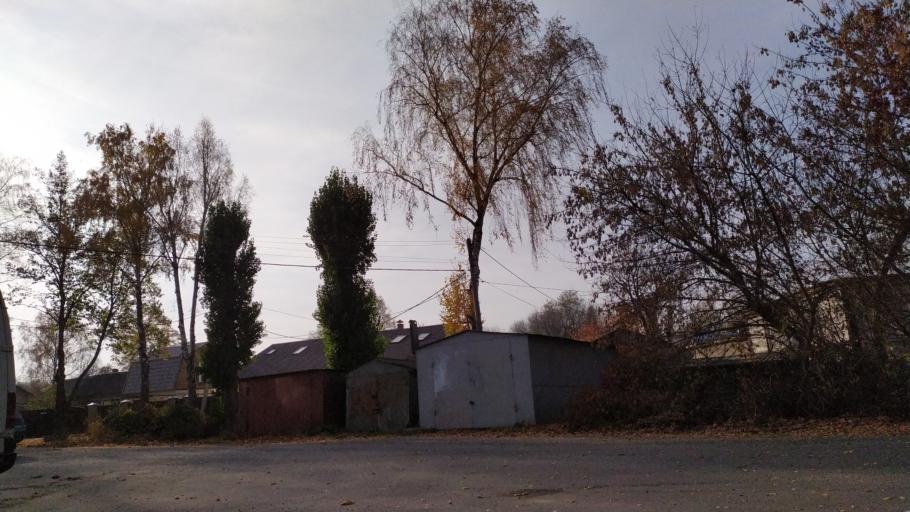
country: RU
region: Kursk
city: Kursk
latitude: 51.6489
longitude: 36.1376
